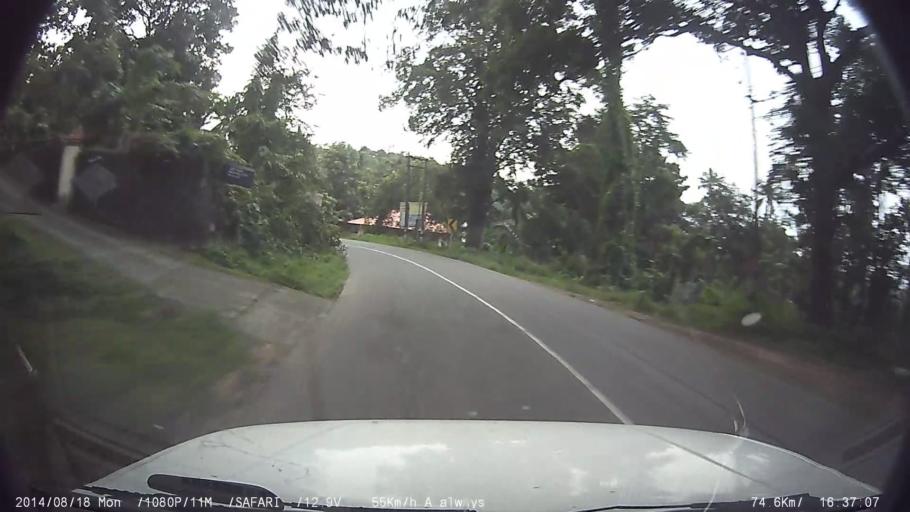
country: IN
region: Kerala
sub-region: Kottayam
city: Palackattumala
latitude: 9.8201
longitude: 76.5860
